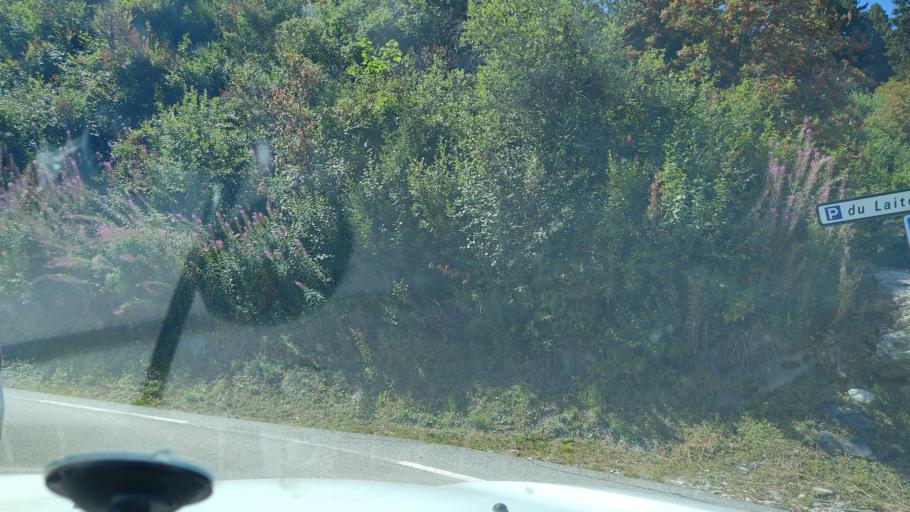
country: FR
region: Rhone-Alpes
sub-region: Departement de la Savoie
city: Meribel
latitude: 45.3754
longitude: 6.5716
